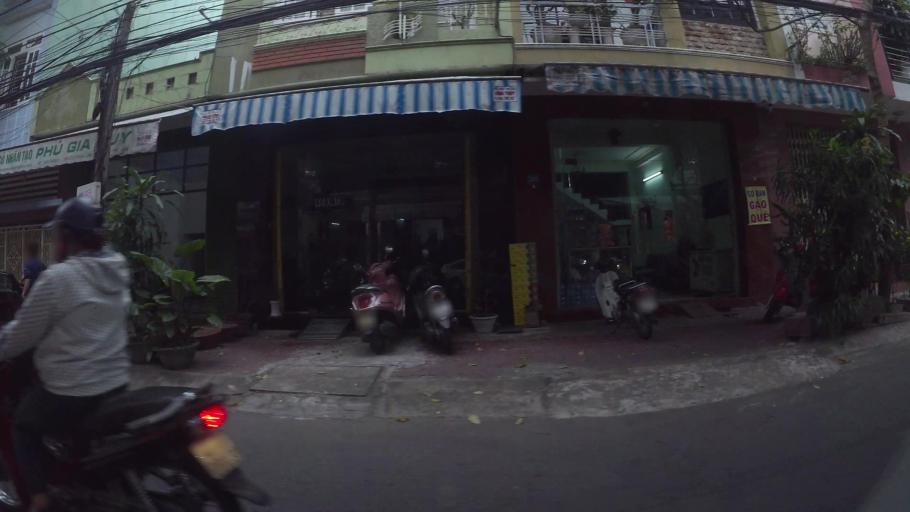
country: VN
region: Da Nang
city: Thanh Khe
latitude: 16.0642
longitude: 108.1829
